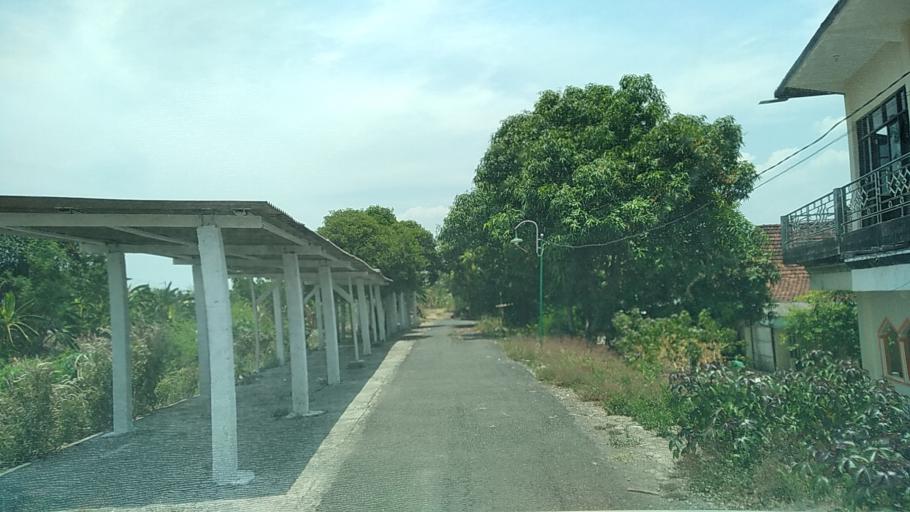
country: ID
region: Central Java
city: Mranggen
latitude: -6.9660
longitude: 110.4970
